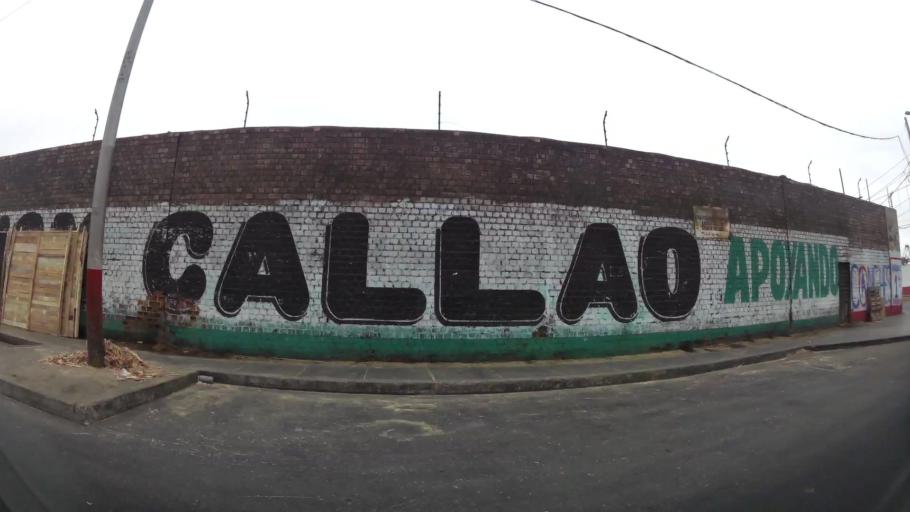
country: PE
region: Callao
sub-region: Callao
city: Callao
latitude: -12.0519
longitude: -77.1408
